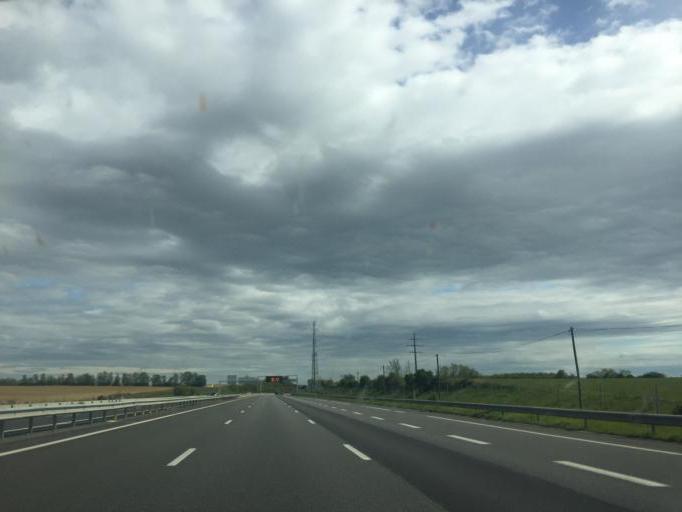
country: FR
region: Rhone-Alpes
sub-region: Departement du Rhone
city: Montanay
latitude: 45.8810
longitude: 4.8981
